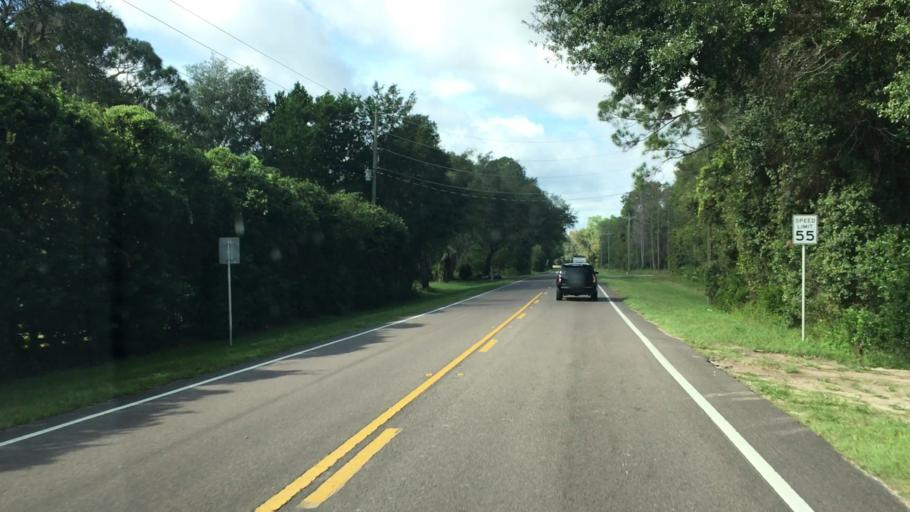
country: US
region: Florida
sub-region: Clay County
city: Keystone Heights
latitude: 29.7351
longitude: -81.9681
